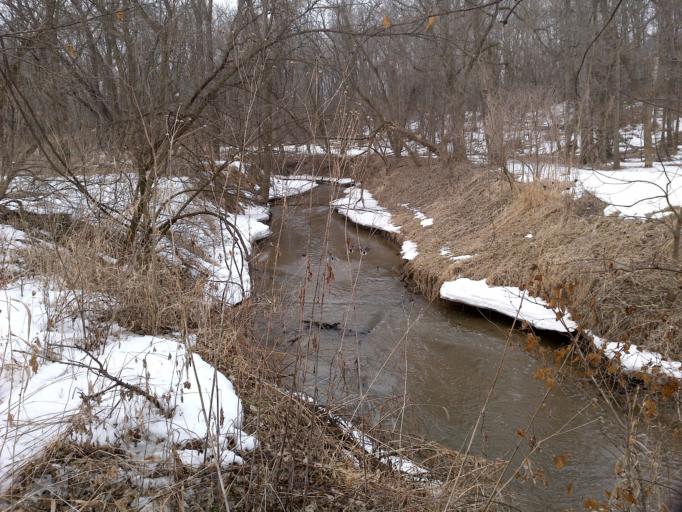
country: US
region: Minnesota
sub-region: Wabasha County
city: Lake City
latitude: 44.4546
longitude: -92.2936
